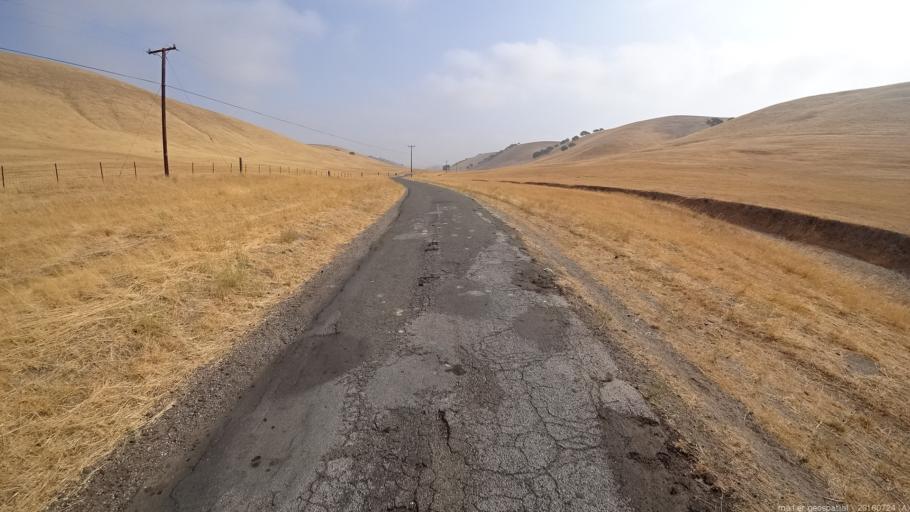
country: US
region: California
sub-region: San Luis Obispo County
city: San Miguel
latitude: 35.8743
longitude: -120.7920
